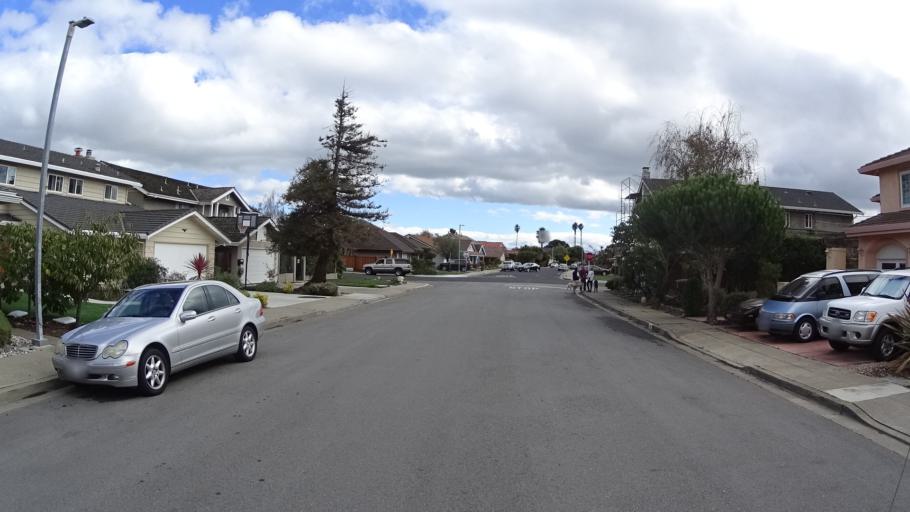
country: US
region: California
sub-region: San Mateo County
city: Foster City
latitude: 37.5644
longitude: -122.2639
